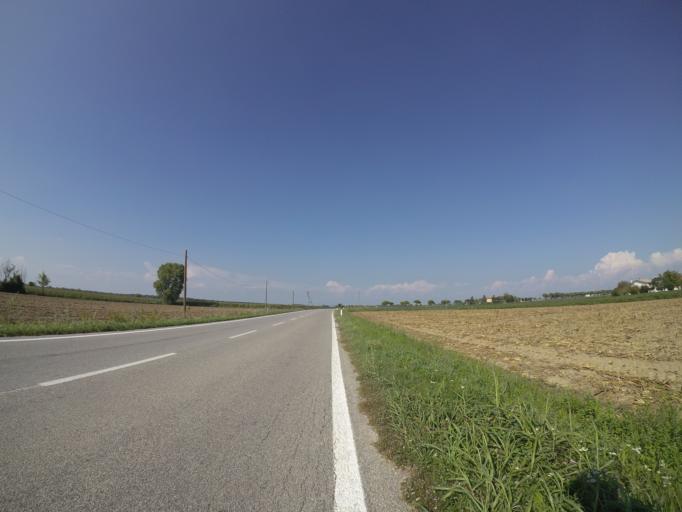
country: IT
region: Friuli Venezia Giulia
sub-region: Provincia di Udine
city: Marano Lagunare
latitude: 45.7836
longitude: 13.1632
